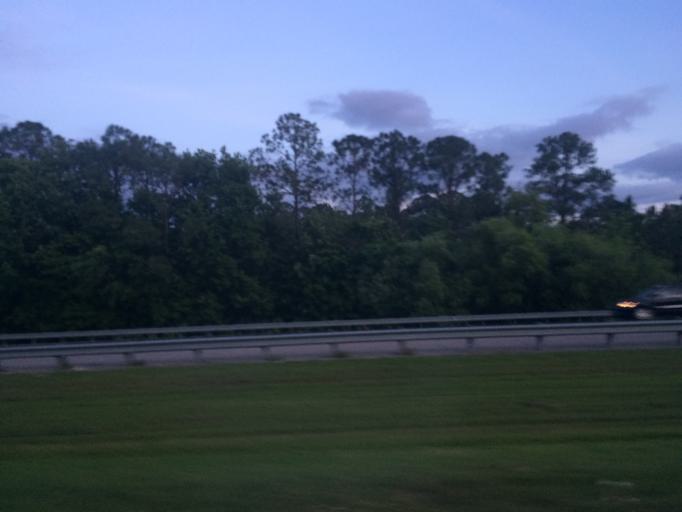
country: US
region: Florida
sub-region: Osceola County
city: Celebration
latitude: 28.2967
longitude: -81.5794
